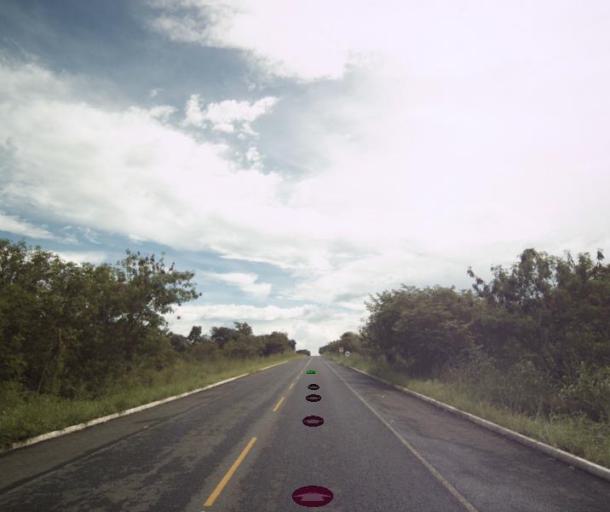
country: BR
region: Goias
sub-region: Sao Miguel Do Araguaia
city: Sao Miguel do Araguaia
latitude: -13.2879
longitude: -50.1990
